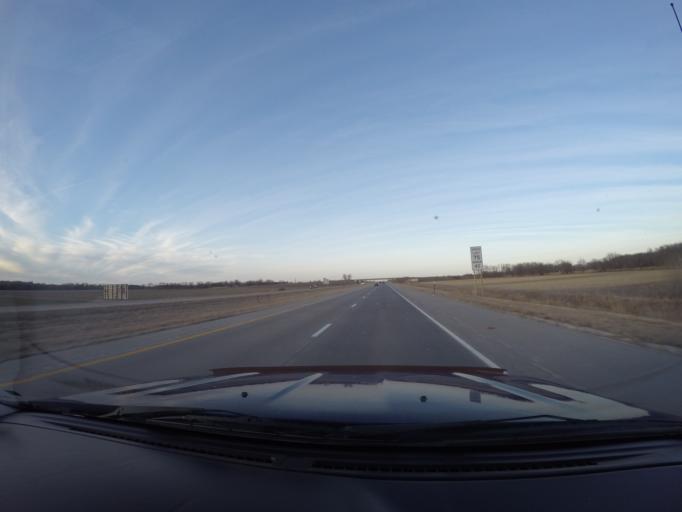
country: US
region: Kansas
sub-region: McPherson County
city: Lindsborg
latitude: 38.6338
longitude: -97.6213
